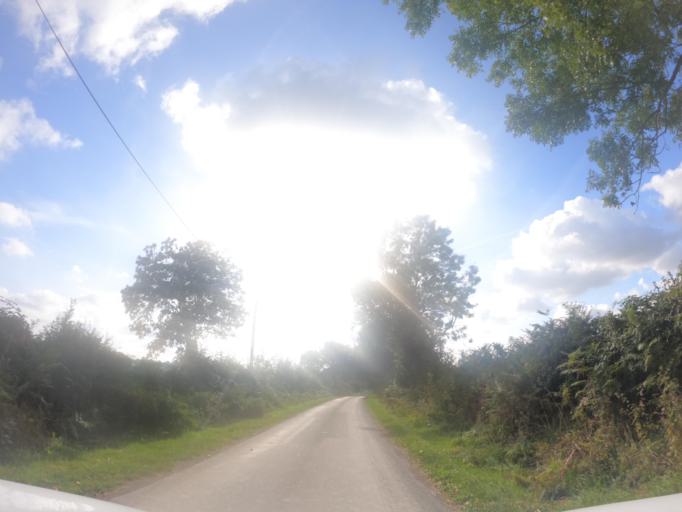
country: FR
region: Poitou-Charentes
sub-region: Departement des Deux-Sevres
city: Courlay
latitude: 46.7767
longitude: -0.5980
